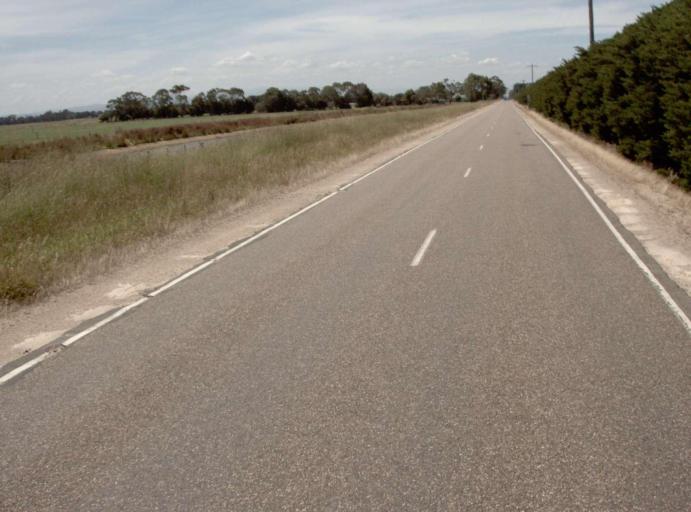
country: AU
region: Victoria
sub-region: Wellington
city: Heyfield
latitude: -38.0519
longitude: 146.8747
